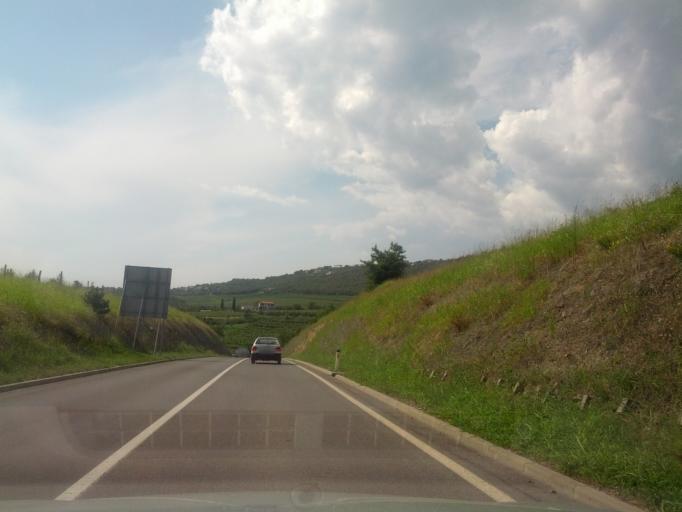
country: SI
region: Koper-Capodistria
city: Spodnje Skofije
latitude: 45.5677
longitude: 13.7821
